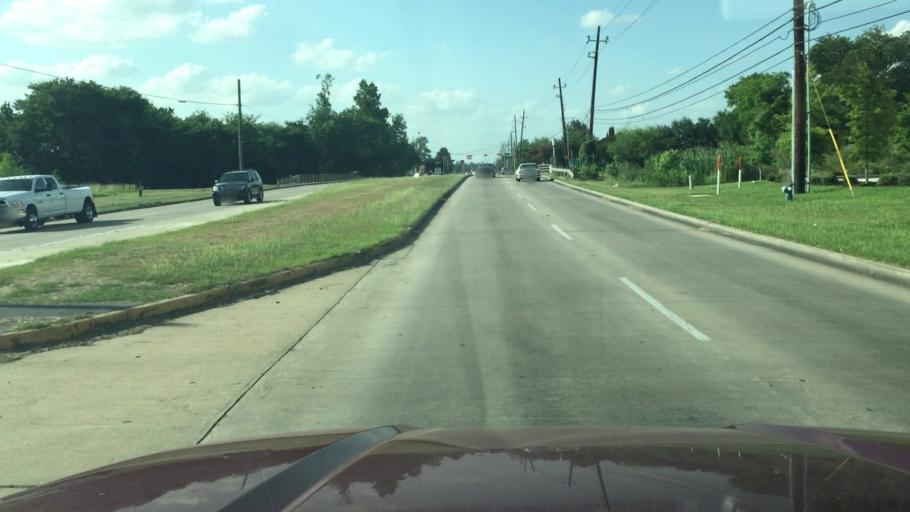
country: US
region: Texas
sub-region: Harris County
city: Hudson
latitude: 29.9476
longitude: -95.4981
